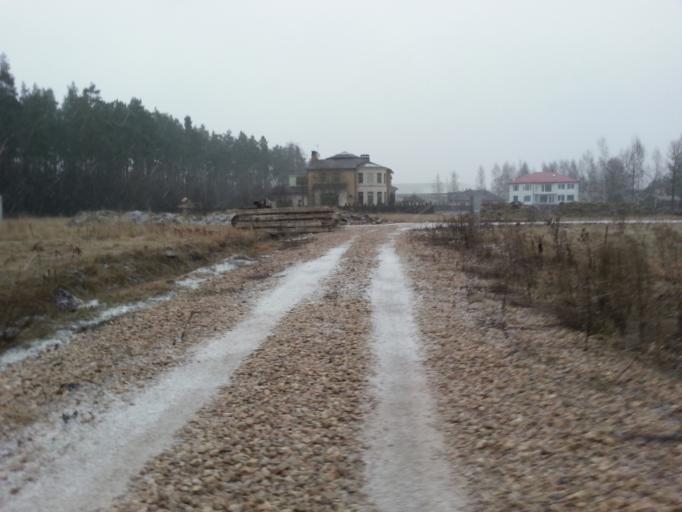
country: LV
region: Stopini
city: Ulbroka
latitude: 56.9385
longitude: 24.2359
